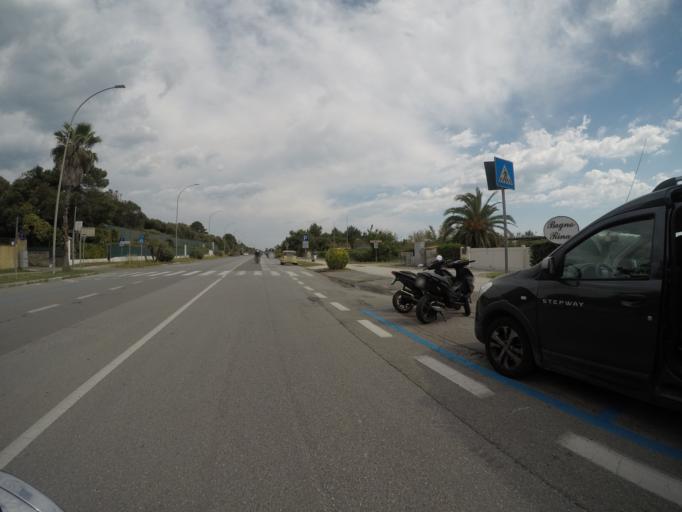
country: IT
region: Tuscany
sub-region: Provincia di Massa-Carrara
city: Massa
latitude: 43.9936
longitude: 10.1217
